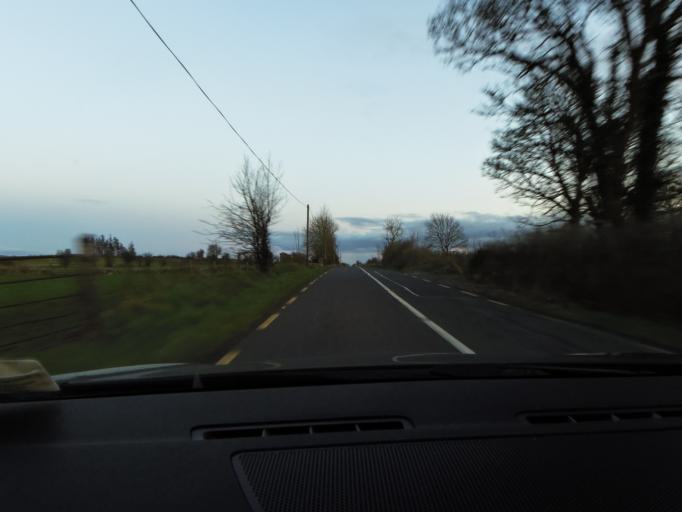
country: IE
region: Connaught
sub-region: Roscommon
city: Boyle
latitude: 53.8591
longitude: -8.2332
